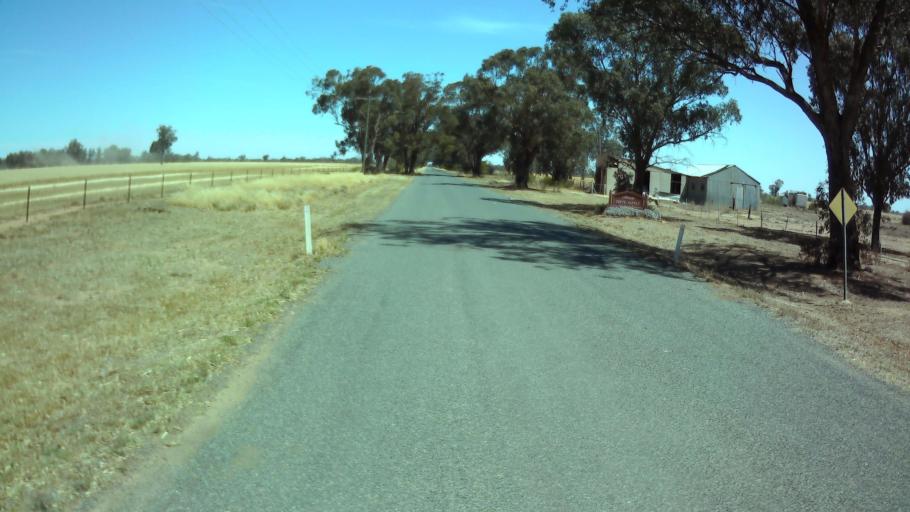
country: AU
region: New South Wales
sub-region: Weddin
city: Grenfell
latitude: -34.0155
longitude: 147.7937
